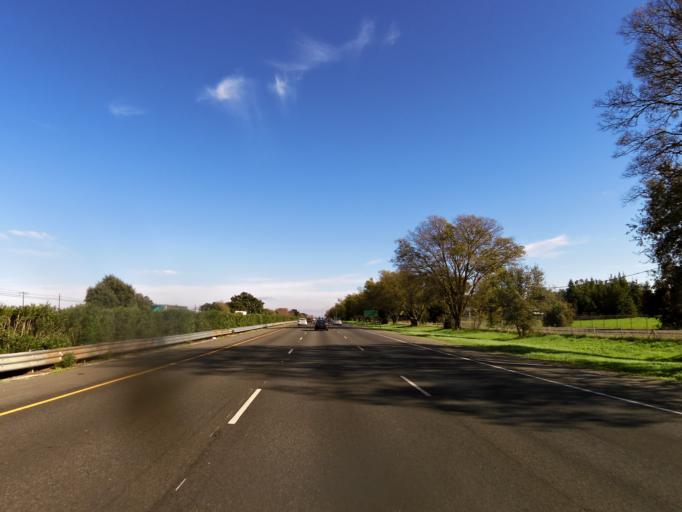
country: US
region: California
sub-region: Yolo County
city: Davis
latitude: 38.5551
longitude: -121.6848
